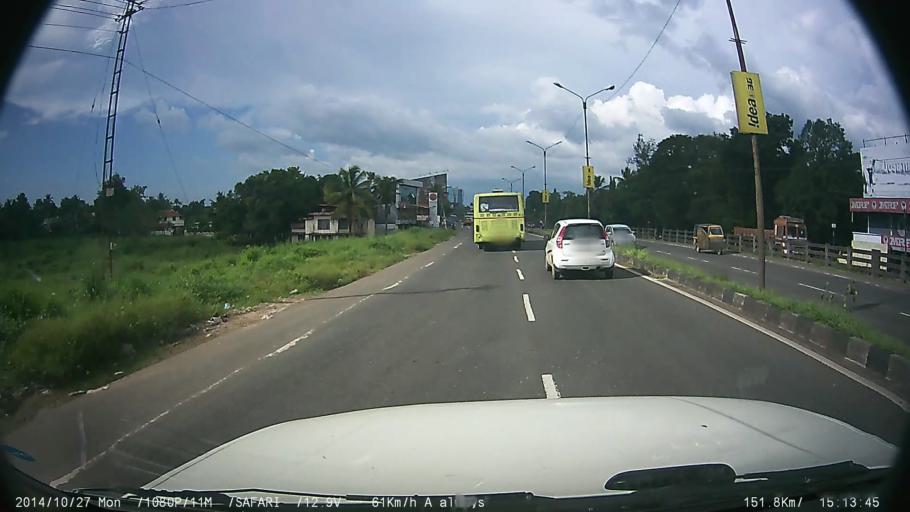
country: IN
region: Kerala
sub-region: Ernakulam
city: Aluva
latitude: 10.1398
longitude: 76.3535
